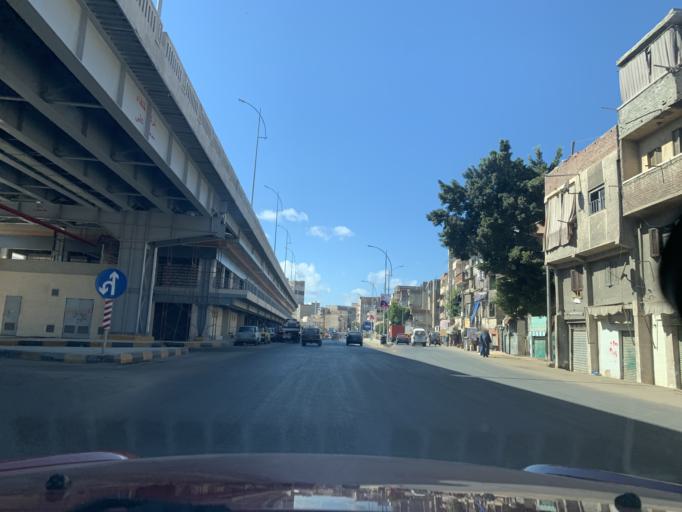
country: EG
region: Alexandria
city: Alexandria
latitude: 31.2243
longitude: 29.9827
